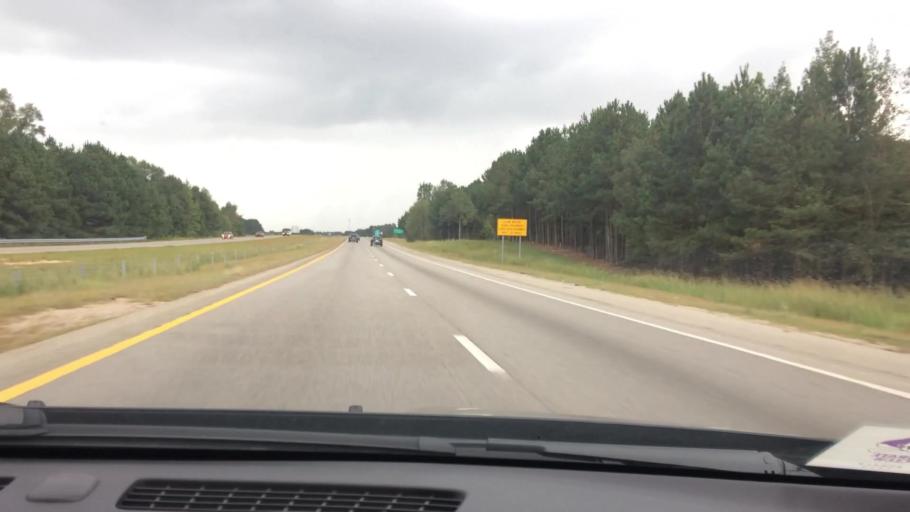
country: US
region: North Carolina
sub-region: Wilson County
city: Lucama
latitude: 35.7270
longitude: -78.0082
